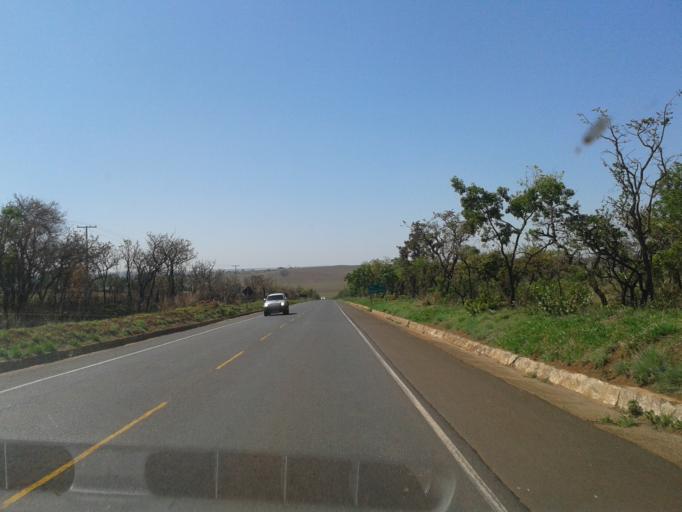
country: BR
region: Minas Gerais
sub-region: Uberlandia
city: Uberlandia
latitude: -19.1048
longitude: -47.9840
